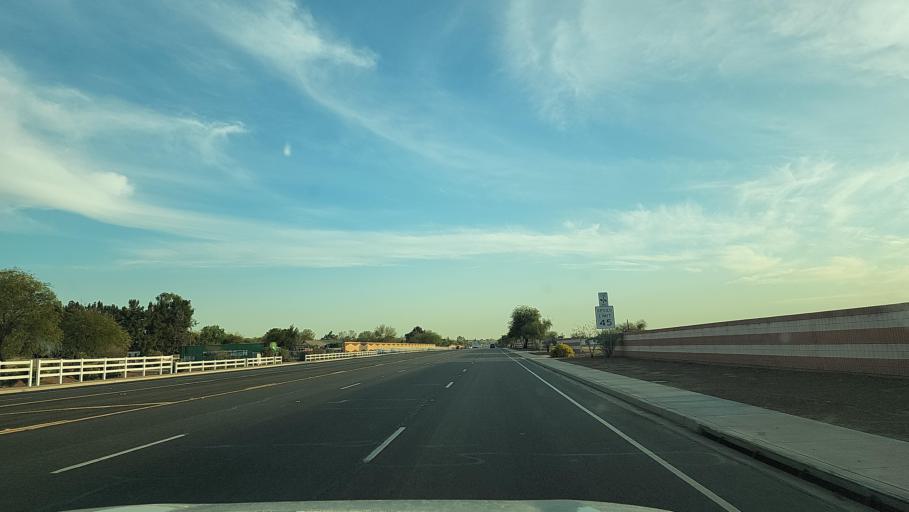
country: US
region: Arizona
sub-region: Maricopa County
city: Mesa
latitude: 33.4799
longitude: -111.7875
